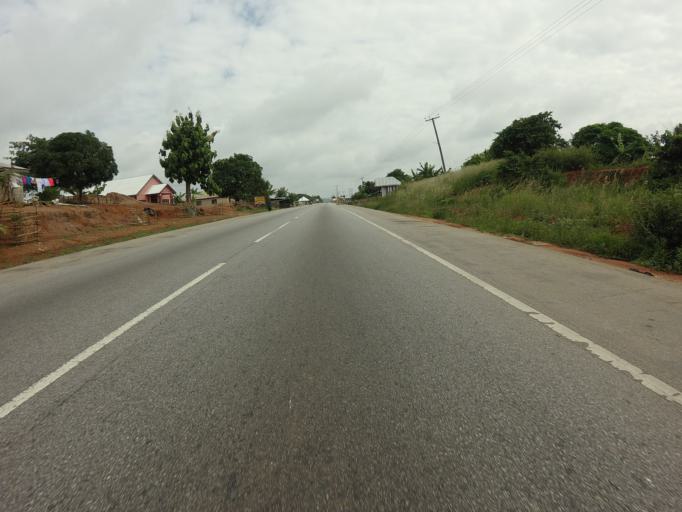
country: GH
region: Ashanti
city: Tafo
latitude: 6.9913
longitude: -1.6932
